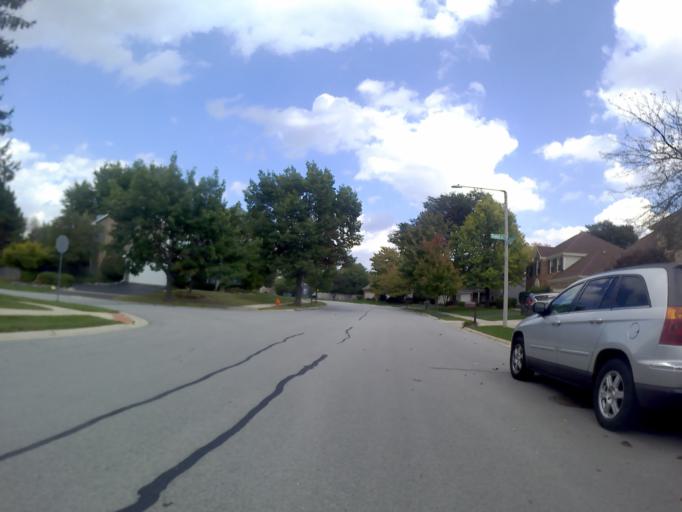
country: US
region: Illinois
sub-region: DuPage County
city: Woodridge
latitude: 41.7367
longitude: -88.0955
